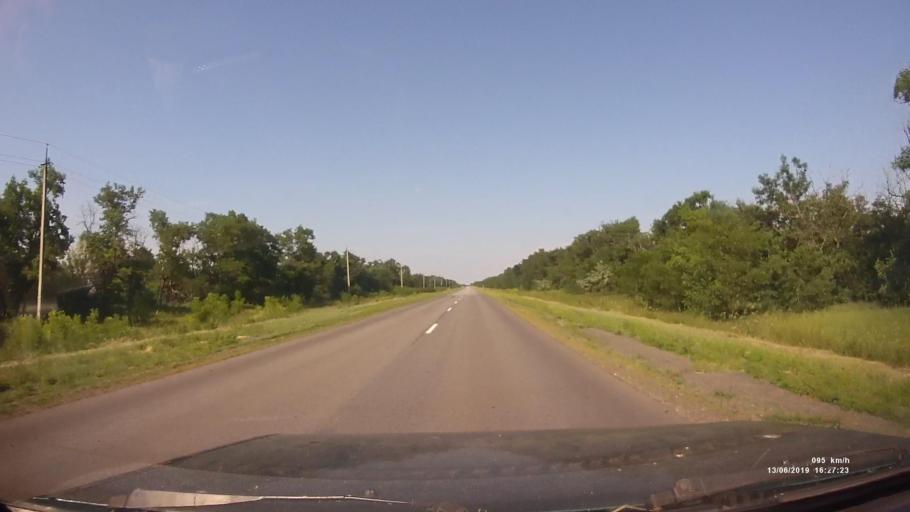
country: RU
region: Rostov
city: Kazanskaya
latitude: 49.8127
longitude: 41.1818
